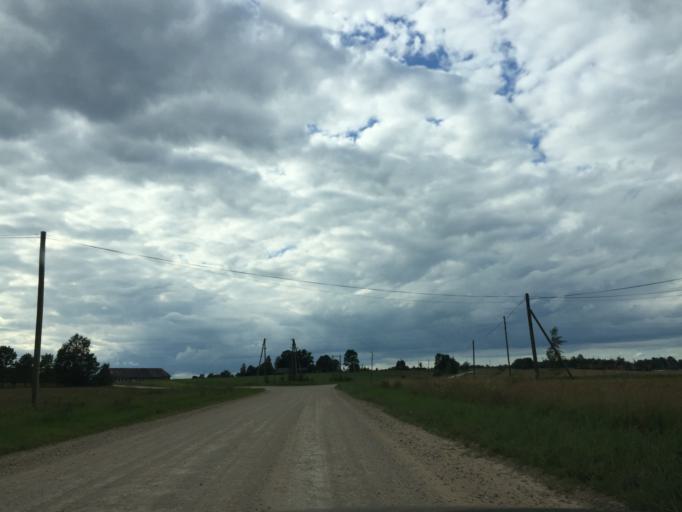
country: LV
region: Malpils
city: Malpils
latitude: 56.9655
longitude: 24.9785
